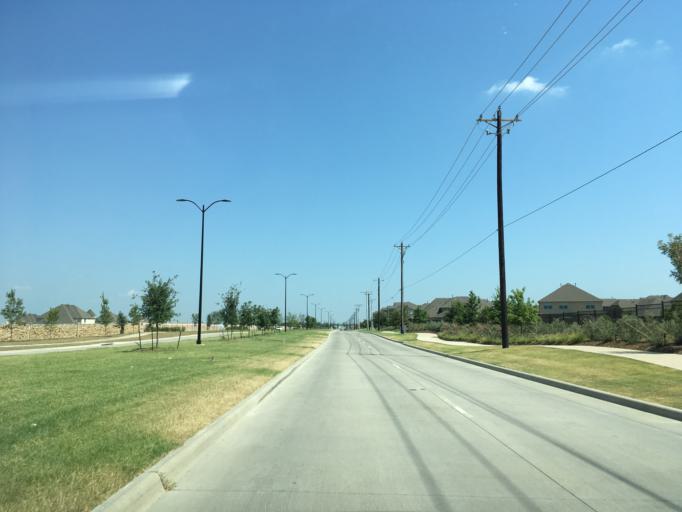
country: US
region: Texas
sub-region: Collin County
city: Prosper
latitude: 33.1954
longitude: -96.7678
